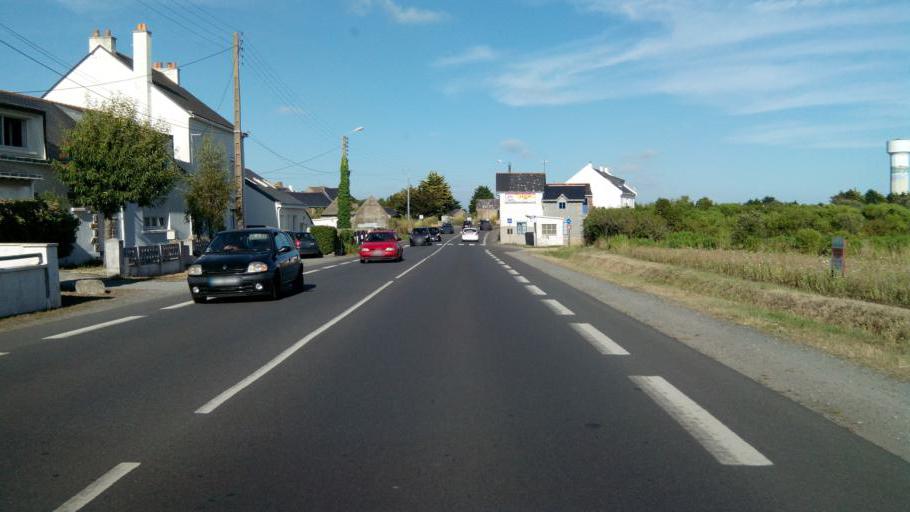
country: FR
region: Pays de la Loire
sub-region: Departement de la Loire-Atlantique
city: Batz-sur-Mer
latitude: 47.2784
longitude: -2.4646
